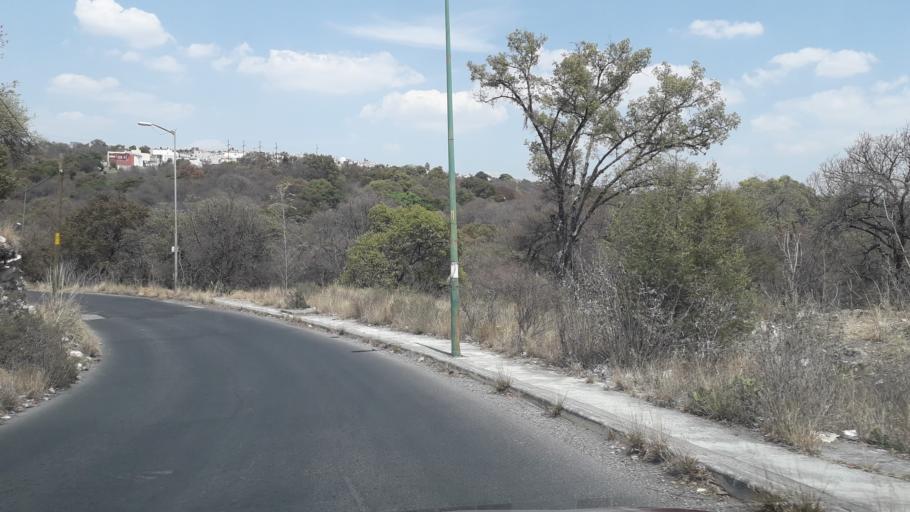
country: MX
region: Puebla
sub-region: Puebla
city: Galaxia la Calera
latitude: 18.9952
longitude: -98.1575
